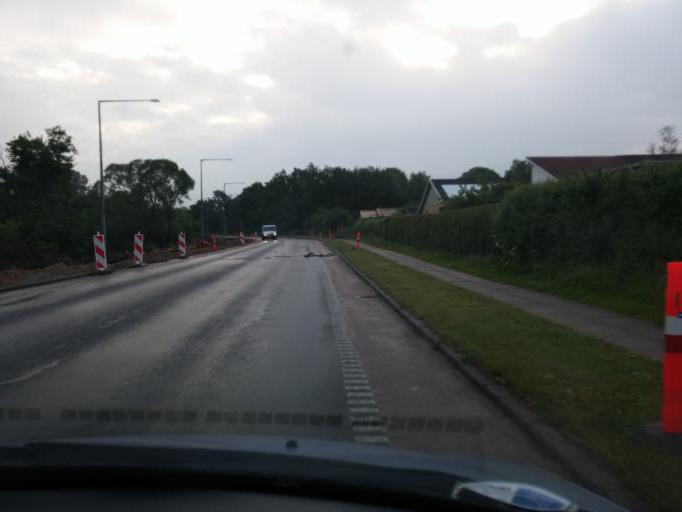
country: DK
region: South Denmark
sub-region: Kerteminde Kommune
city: Munkebo
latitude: 55.4561
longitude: 10.5503
